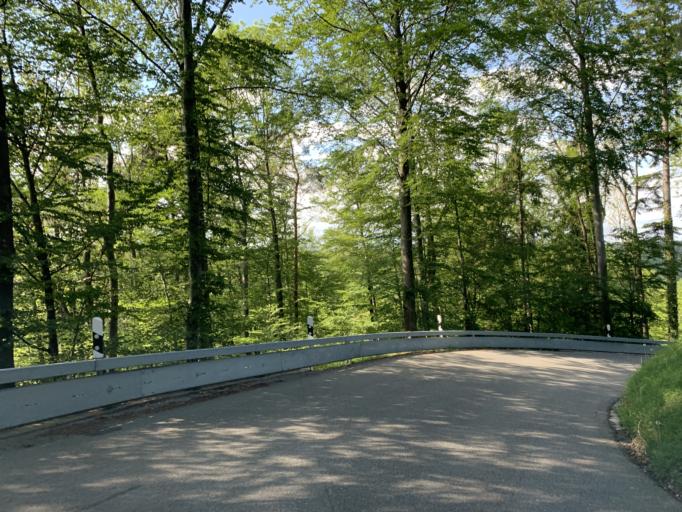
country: CH
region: Zurich
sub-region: Bezirk Winterthur
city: Mattenbach (Kreis 7)
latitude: 47.4604
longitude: 8.7398
